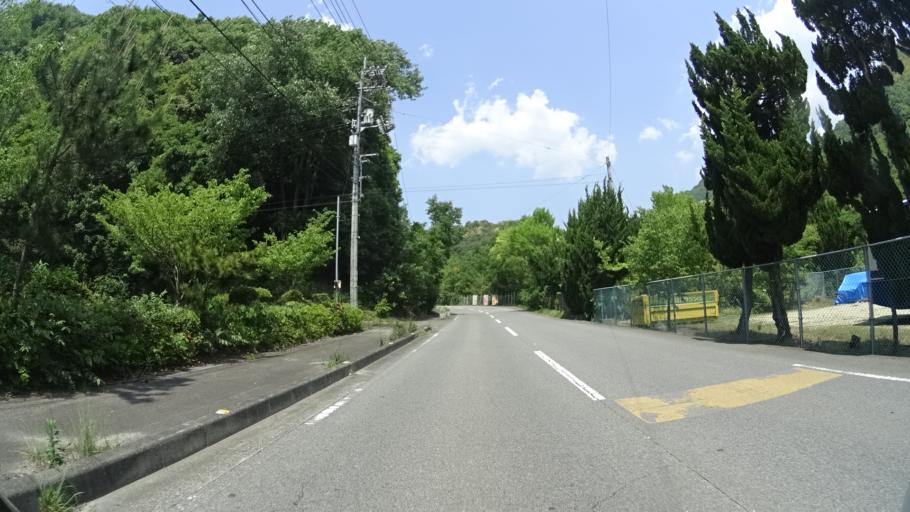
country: JP
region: Ehime
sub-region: Shikoku-chuo Shi
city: Matsuyama
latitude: 33.8672
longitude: 132.8268
